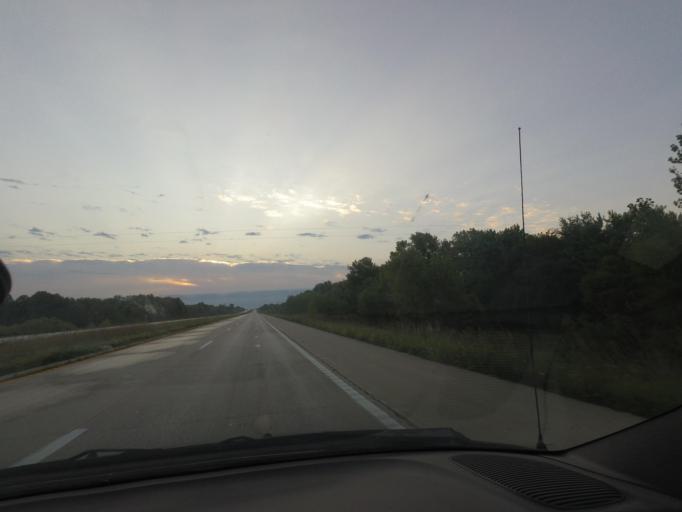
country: US
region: Missouri
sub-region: Macon County
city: Macon
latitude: 39.7528
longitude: -92.4078
